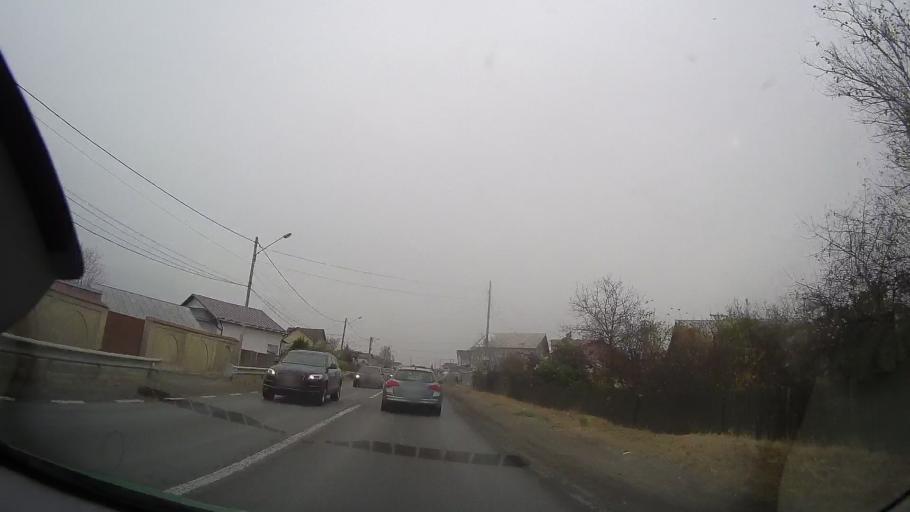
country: RO
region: Prahova
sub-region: Comuna Blejoiu
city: Ploiestiori
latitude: 44.9664
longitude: 26.0292
